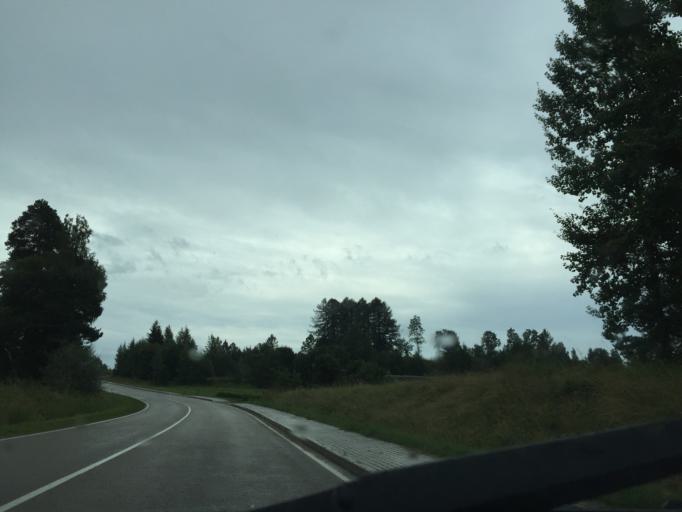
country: LV
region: Preilu Rajons
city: Jaunaglona
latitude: 56.2392
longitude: 27.2204
